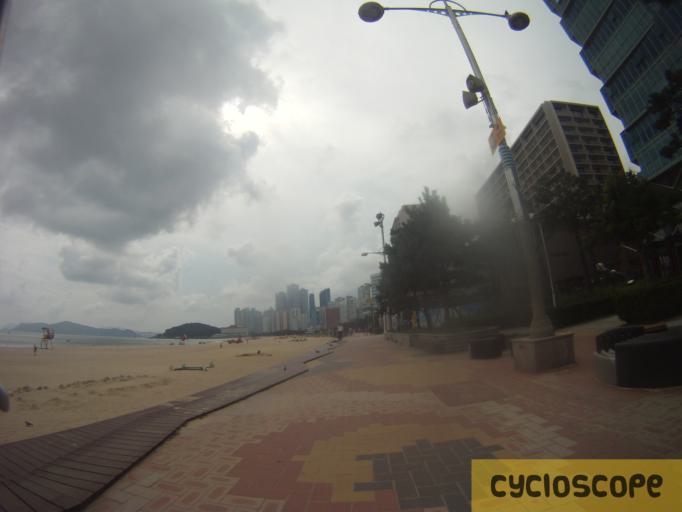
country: KR
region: Busan
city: Kijang
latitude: 35.1598
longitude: 129.1652
